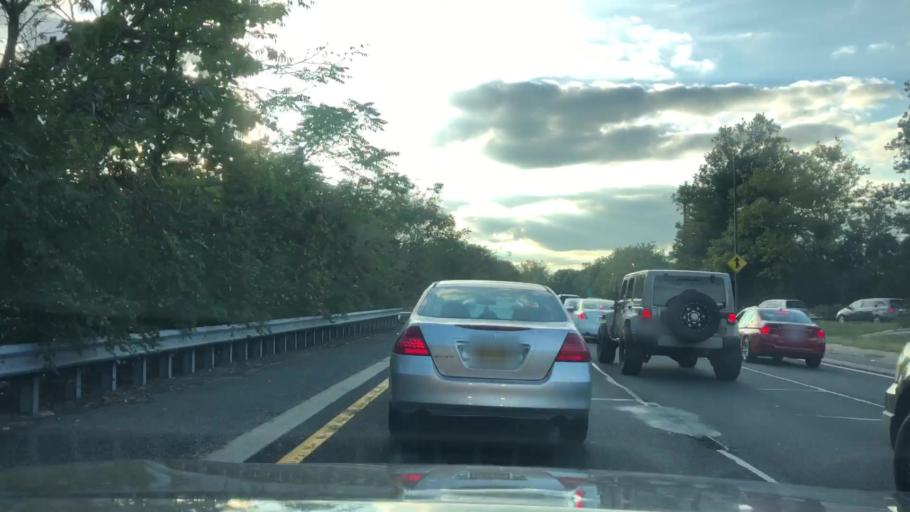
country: US
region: New York
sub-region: Nassau County
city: Roosevelt
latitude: 40.6907
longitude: -73.5802
